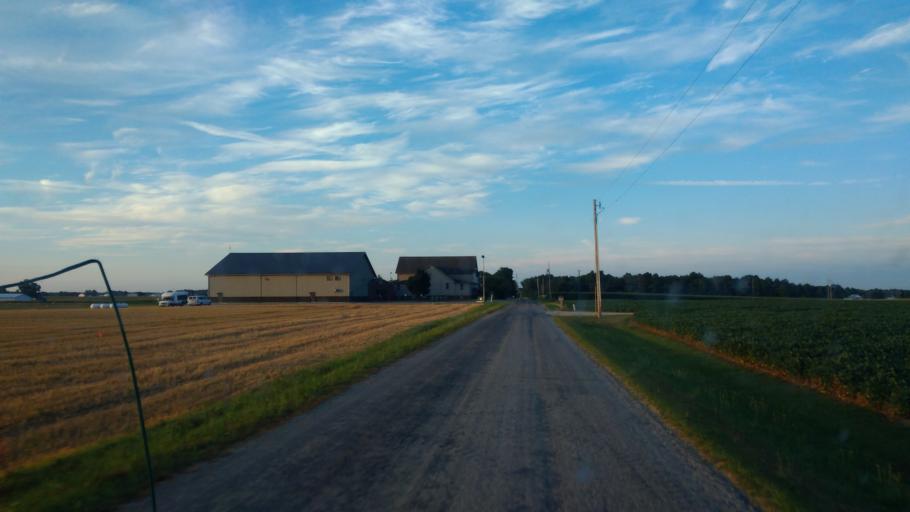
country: US
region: Indiana
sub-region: Adams County
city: Berne
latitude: 40.6652
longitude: -85.0229
